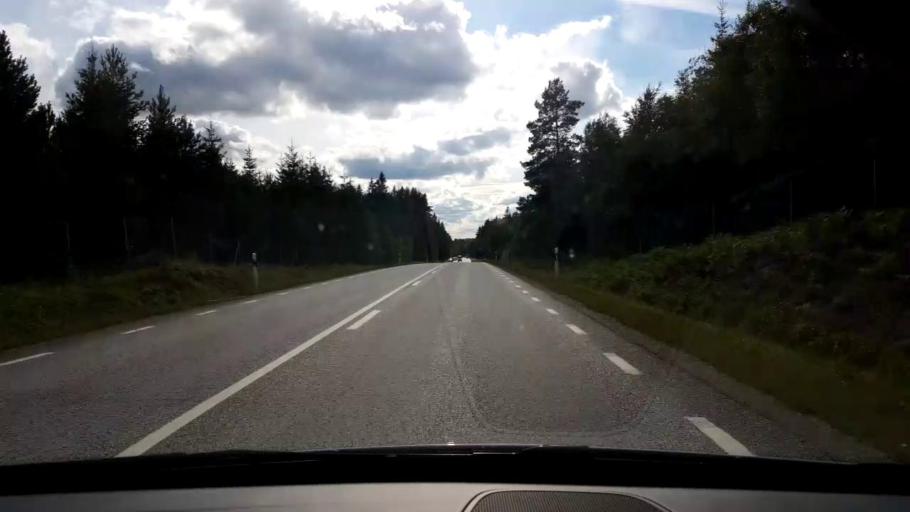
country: SE
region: Joenkoeping
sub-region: Savsjo Kommun
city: Stockaryd
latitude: 57.3744
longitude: 14.5390
